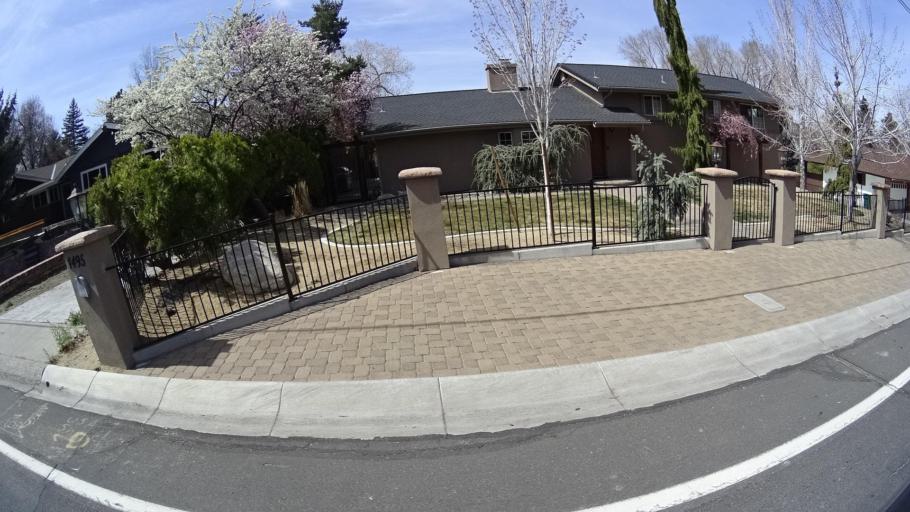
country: US
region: Nevada
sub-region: Washoe County
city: Reno
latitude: 39.4940
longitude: -119.8274
